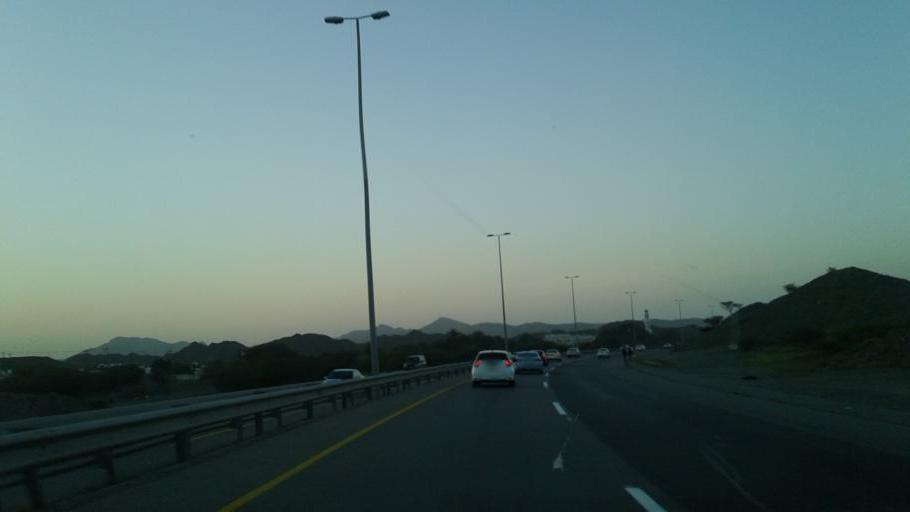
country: OM
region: Muhafazat ad Dakhiliyah
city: Bidbid
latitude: 23.5055
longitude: 58.1928
